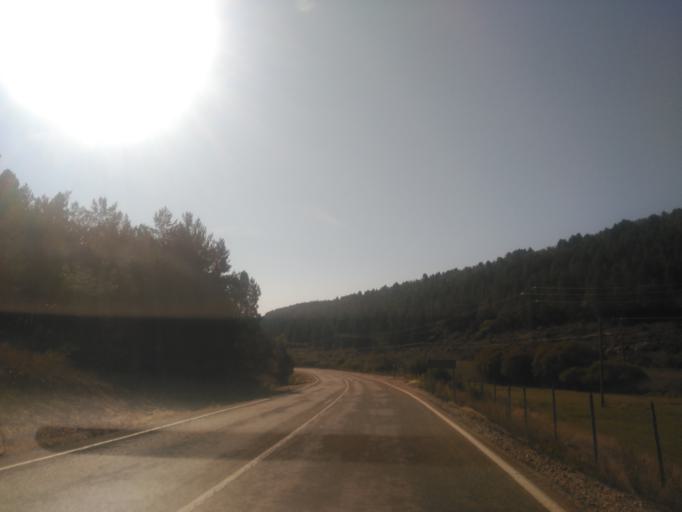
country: ES
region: Castille and Leon
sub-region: Provincia de Soria
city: San Leonardo de Yague
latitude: 41.8155
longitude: -3.0665
